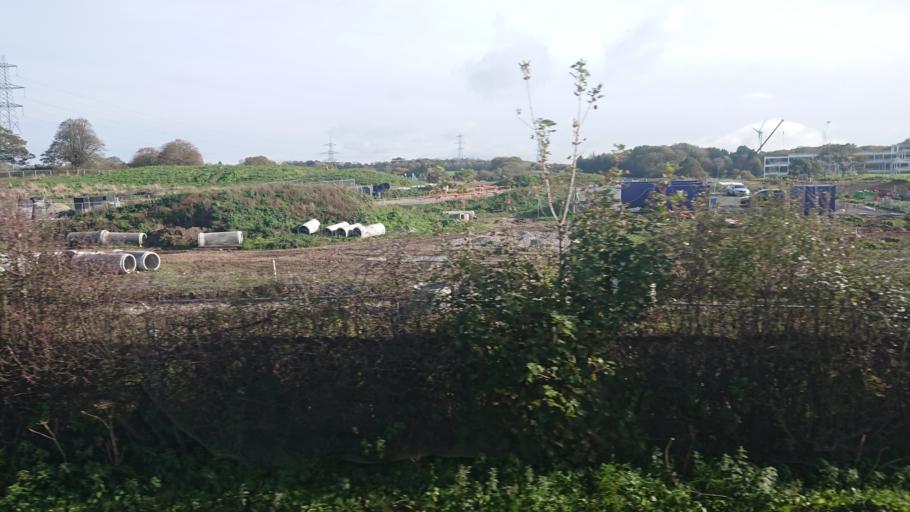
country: GB
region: England
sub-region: Lancashire
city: Lancaster
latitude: 54.0168
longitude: -2.7965
